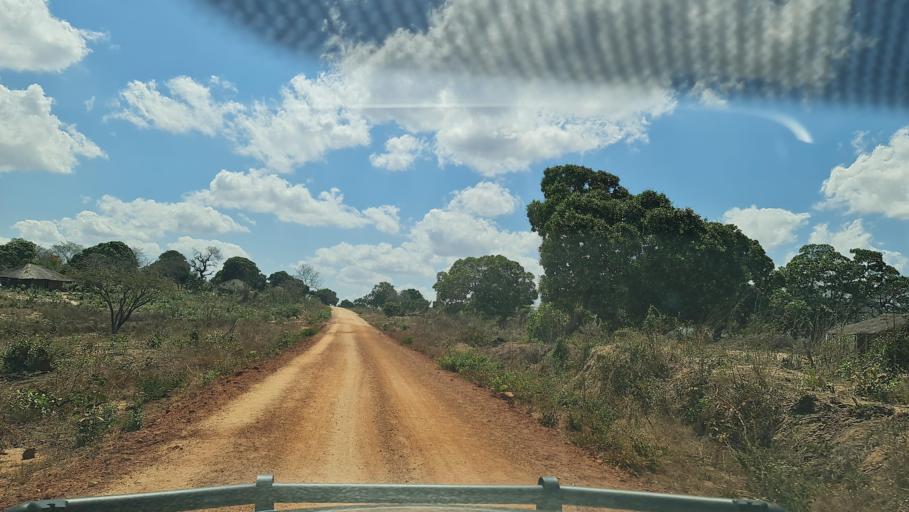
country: MZ
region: Nampula
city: Nacala
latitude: -14.1745
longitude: 40.2375
